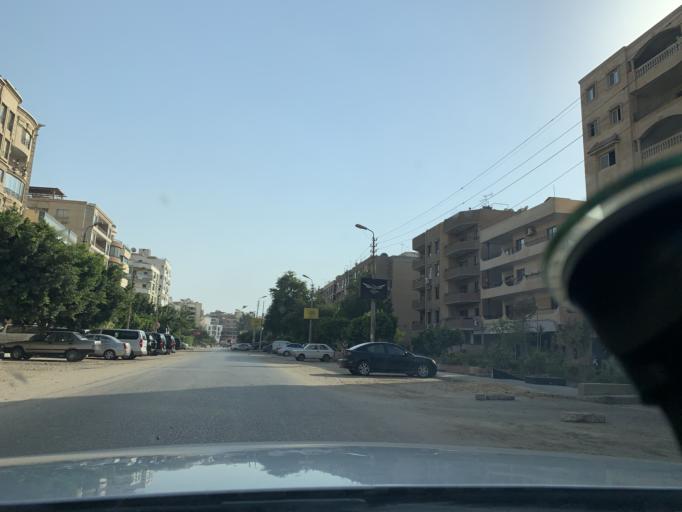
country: EG
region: Muhafazat al Qalyubiyah
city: Al Khankah
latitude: 30.1019
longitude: 31.3775
